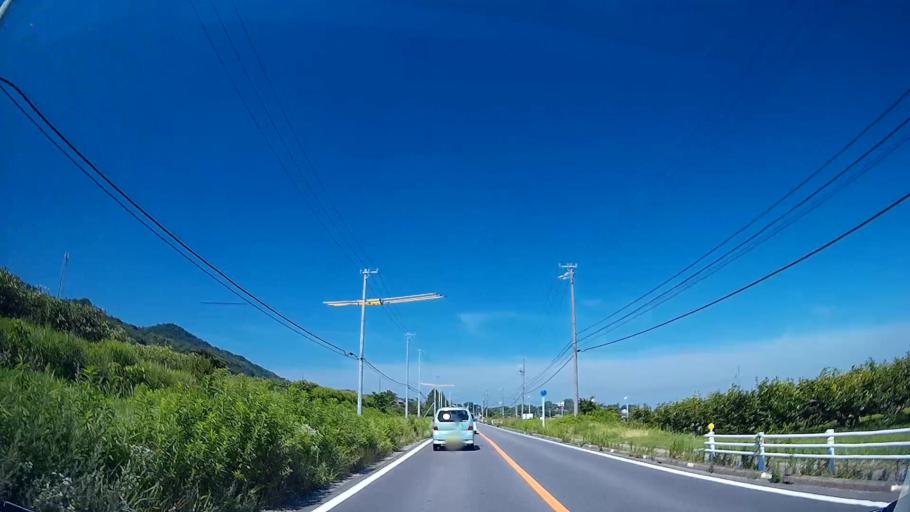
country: JP
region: Aichi
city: Nishio
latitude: 34.8268
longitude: 137.1061
